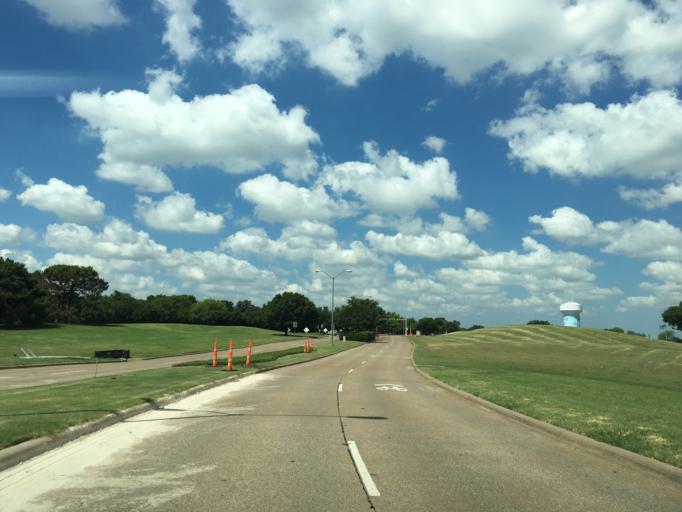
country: US
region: Texas
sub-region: Dallas County
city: Addison
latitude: 32.9267
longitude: -96.8450
